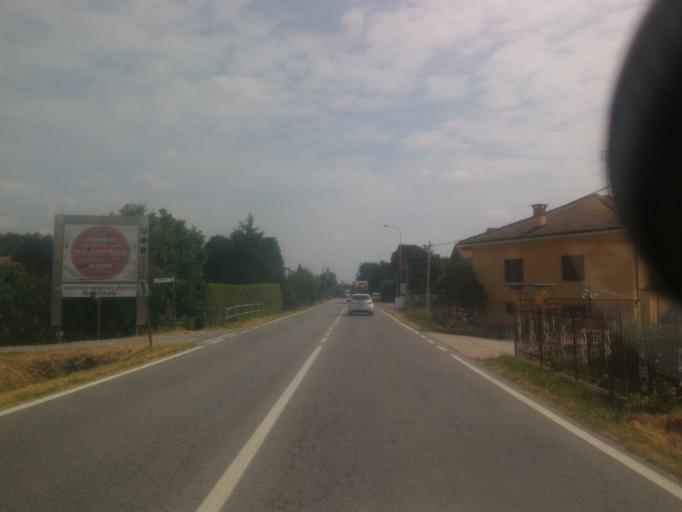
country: IT
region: Piedmont
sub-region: Provincia di Torino
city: Bricherasio
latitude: 44.8425
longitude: 7.3100
